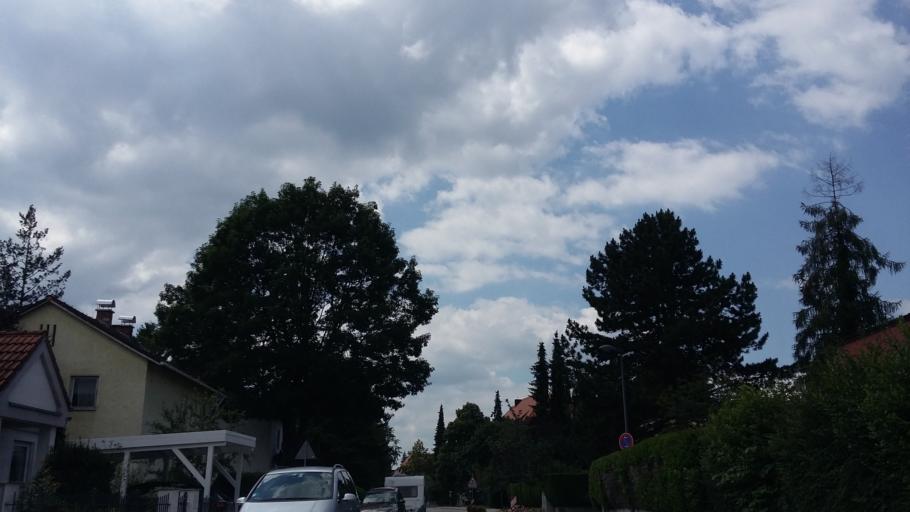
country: DE
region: Bavaria
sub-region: Upper Bavaria
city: Planegg
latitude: 48.1036
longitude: 11.4269
